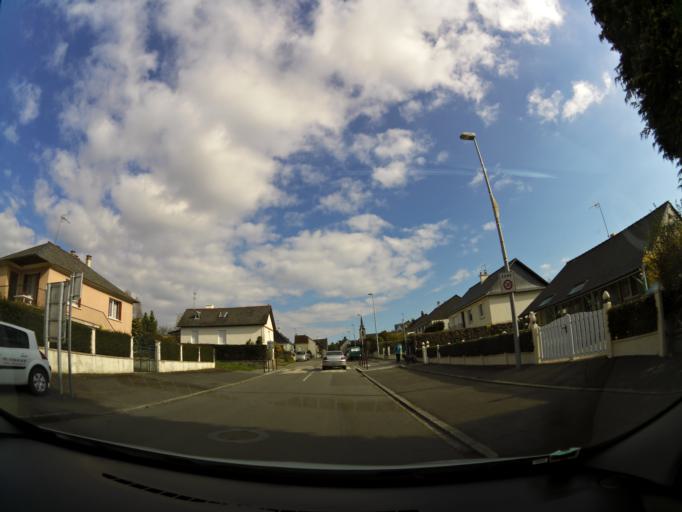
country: FR
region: Brittany
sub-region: Departement d'Ille-et-Vilaine
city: Laille
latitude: 47.9757
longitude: -1.7205
